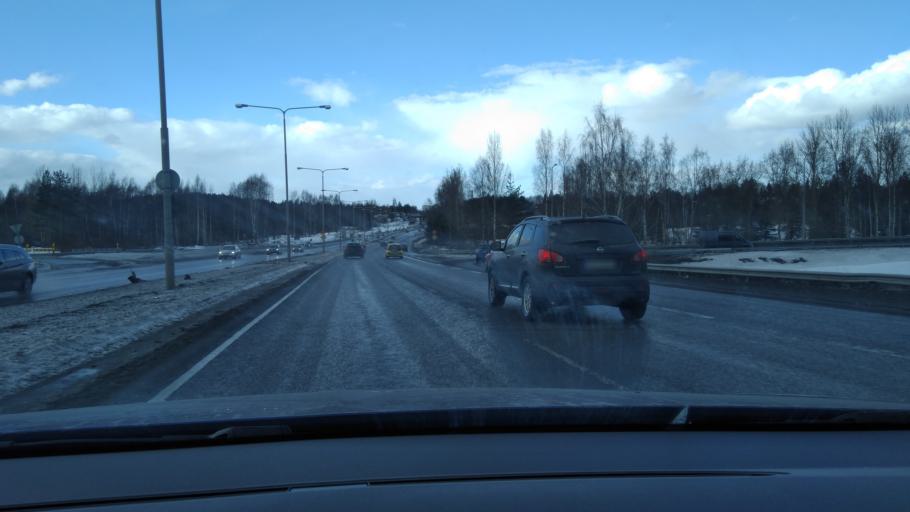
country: FI
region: Pirkanmaa
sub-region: Tampere
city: Tampere
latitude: 61.4799
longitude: 23.8307
